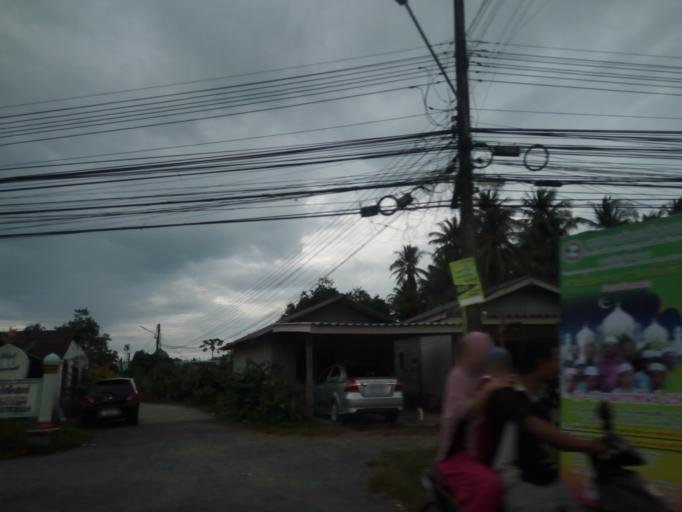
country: TH
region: Phuket
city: Thalang
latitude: 8.0734
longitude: 98.3873
